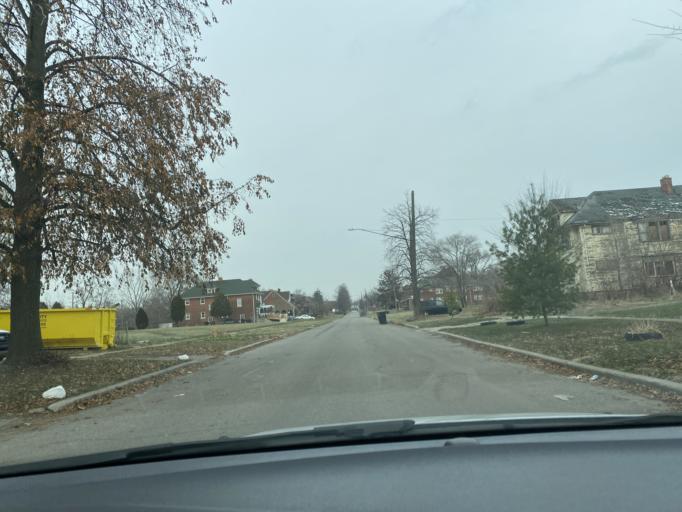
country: US
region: Michigan
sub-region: Wayne County
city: Highland Park
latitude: 42.3690
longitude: -83.1253
